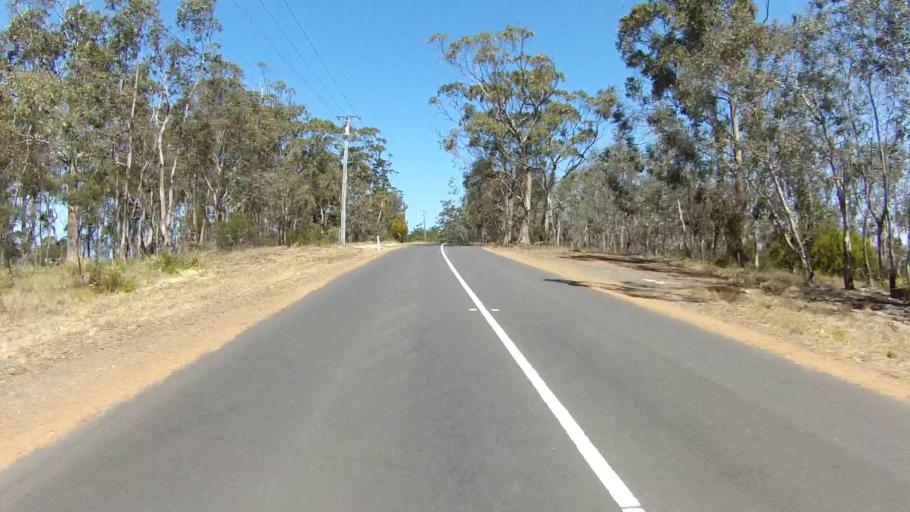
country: AU
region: Tasmania
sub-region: Clarence
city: Sandford
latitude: -43.0114
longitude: 147.4805
